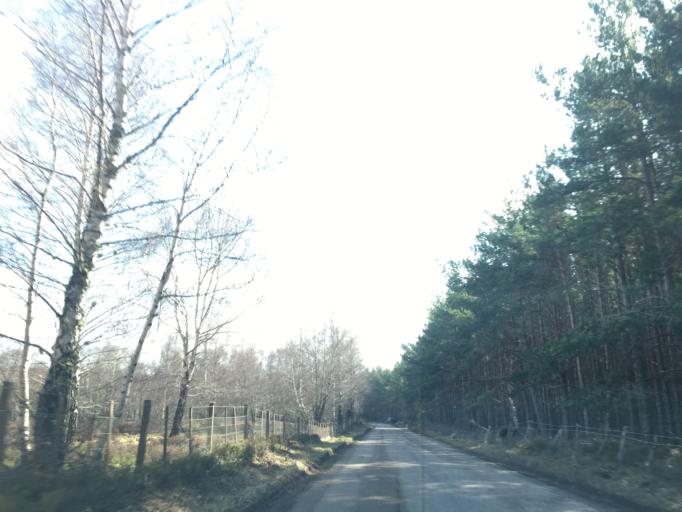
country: GB
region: Scotland
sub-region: Highland
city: Kingussie
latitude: 57.0703
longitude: -4.0060
